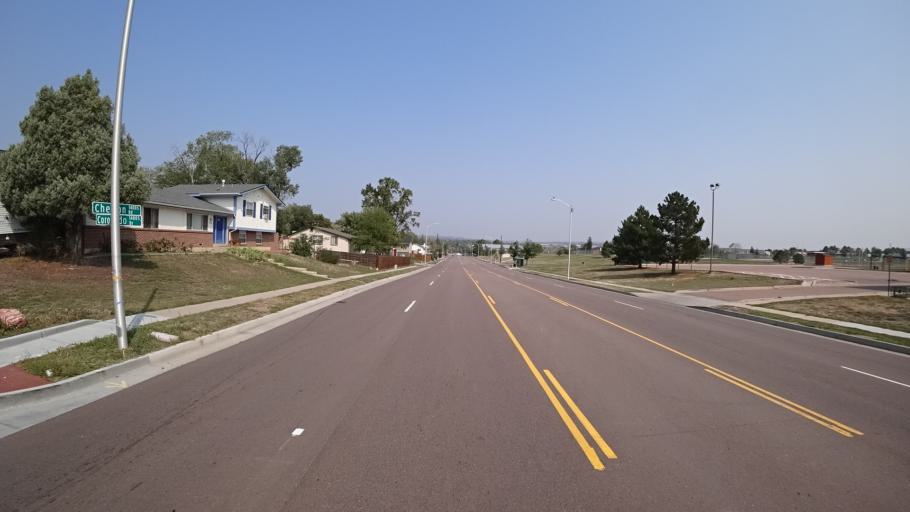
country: US
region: Colorado
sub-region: El Paso County
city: Stratmoor
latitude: 38.8116
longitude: -104.7664
